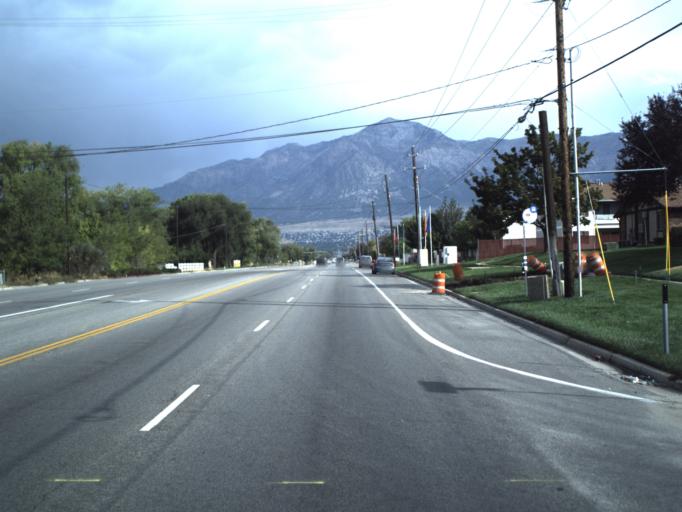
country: US
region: Utah
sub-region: Weber County
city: Harrisville
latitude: 41.2696
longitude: -111.9694
